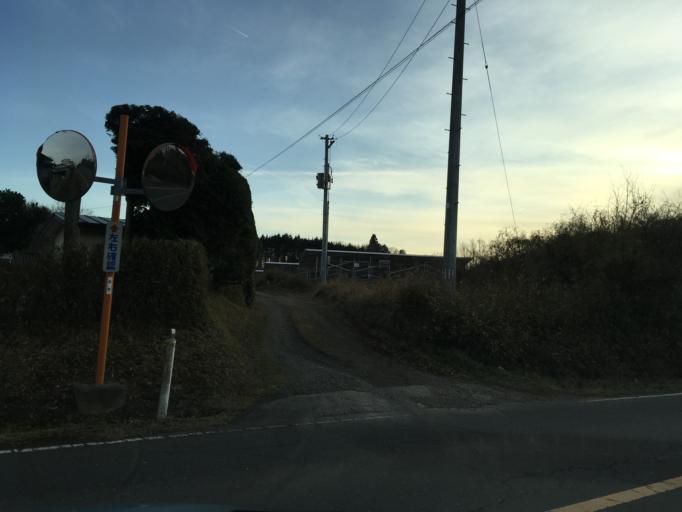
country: JP
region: Miyagi
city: Kogota
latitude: 38.6707
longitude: 141.0857
